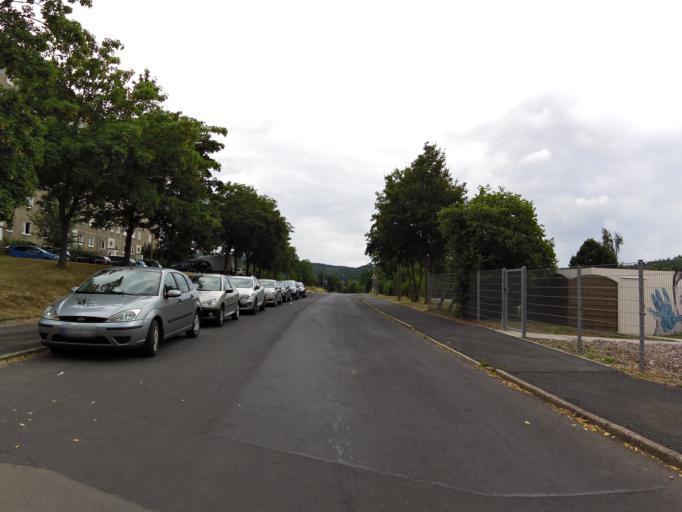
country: DE
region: Thuringia
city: Bad Salzungen
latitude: 50.8082
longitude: 10.2541
